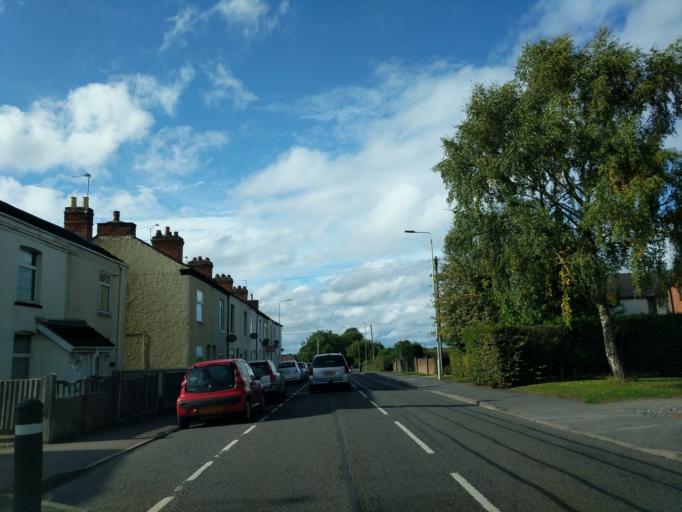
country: GB
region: England
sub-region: Leicestershire
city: Coalville
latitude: 52.7011
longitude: -1.3695
